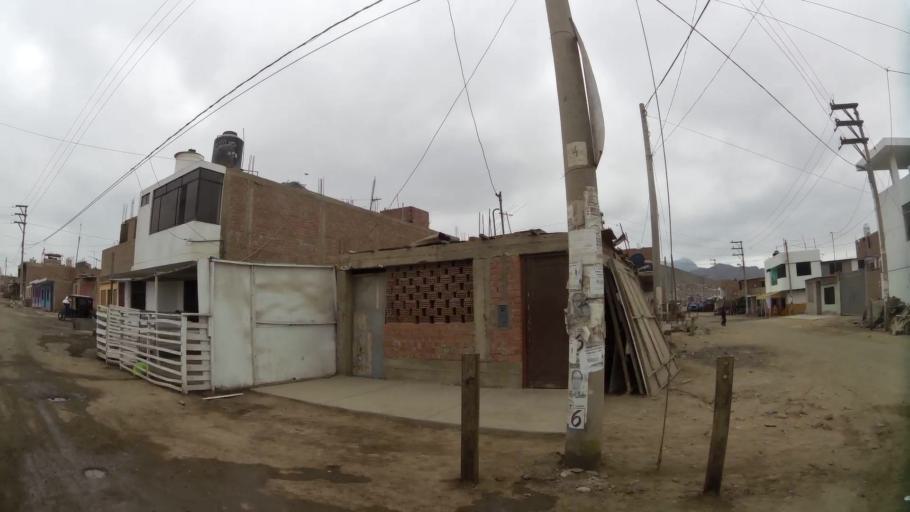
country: PE
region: Lima
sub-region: Lima
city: Pucusana
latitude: -12.4696
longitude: -76.7526
